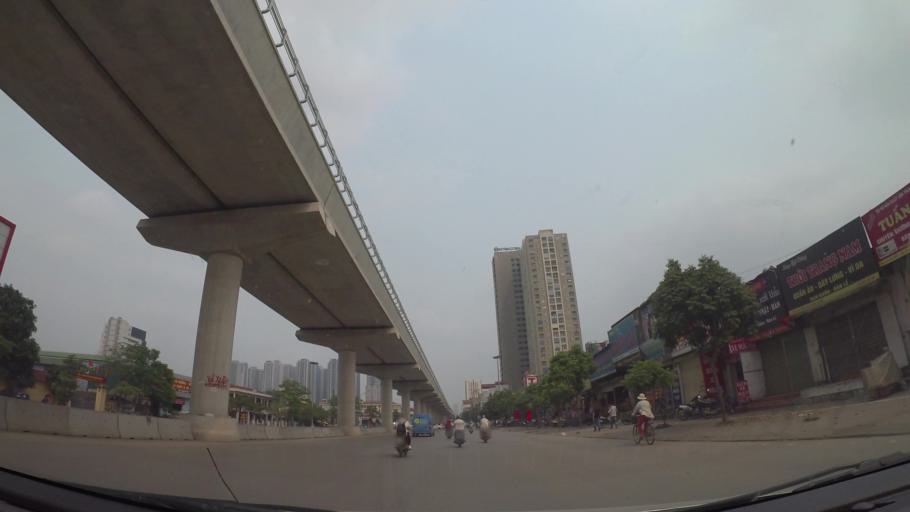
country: VN
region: Ha Noi
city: Cau Dien
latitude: 21.0430
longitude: 105.7573
